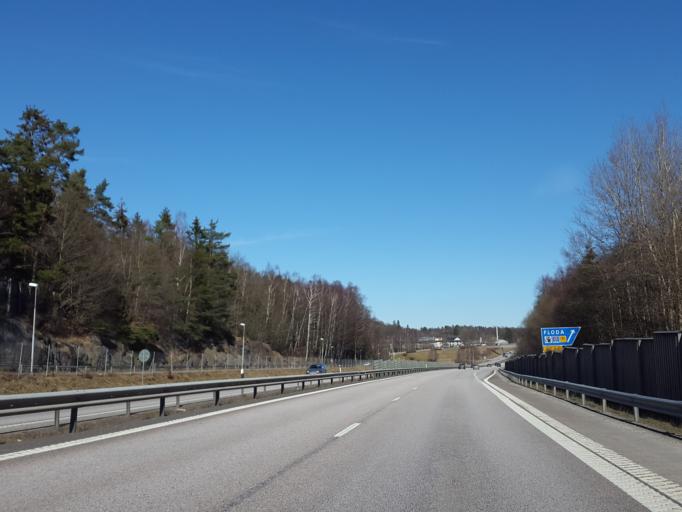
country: SE
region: Vaestra Goetaland
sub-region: Lerums Kommun
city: Stenkullen
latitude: 57.7986
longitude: 12.3588
